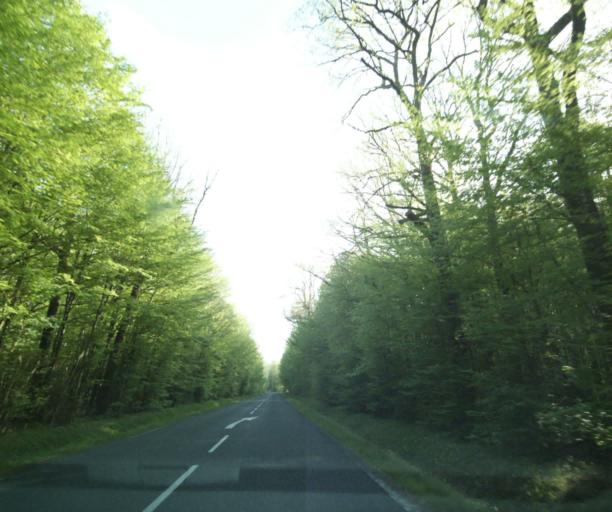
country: FR
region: Ile-de-France
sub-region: Departement de Seine-et-Marne
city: La Chapelle-Gauthier
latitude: 48.5112
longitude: 2.9290
